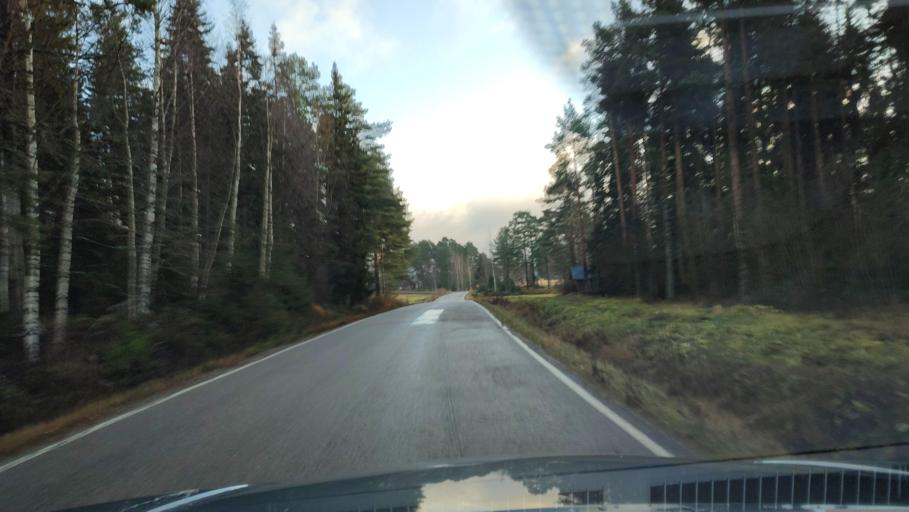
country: FI
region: Ostrobothnia
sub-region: Sydosterbotten
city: Naerpes
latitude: 62.4440
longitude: 21.4079
